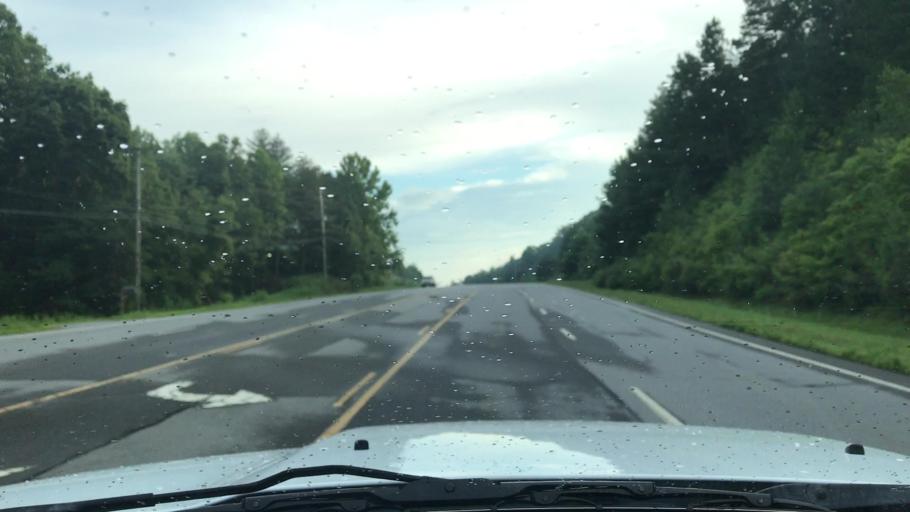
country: US
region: North Carolina
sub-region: Cherokee County
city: Murphy
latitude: 35.0117
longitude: -84.1257
